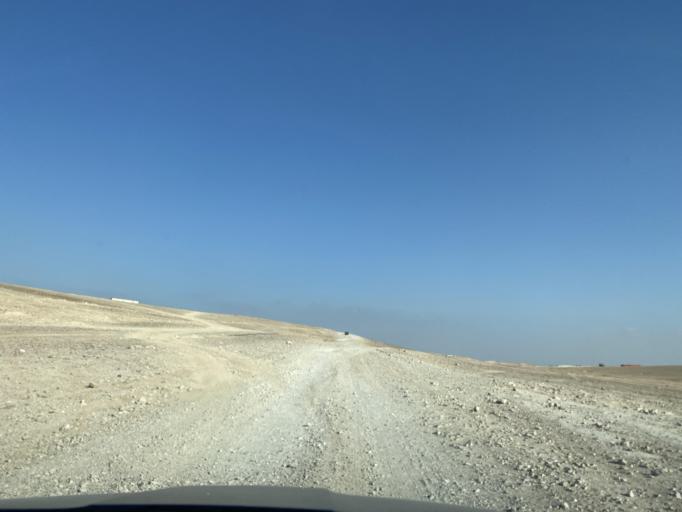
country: PS
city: `Arab ar Rashaydah
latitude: 31.5247
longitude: 35.2975
